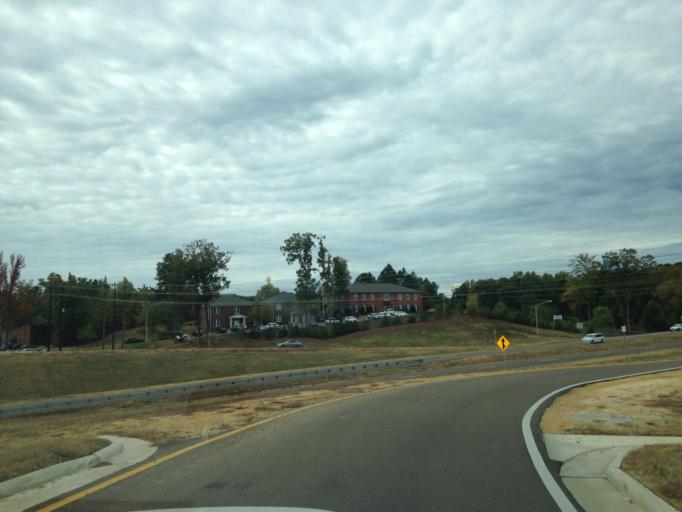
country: US
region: Mississippi
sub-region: Lafayette County
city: University
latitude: 34.3560
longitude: -89.5329
